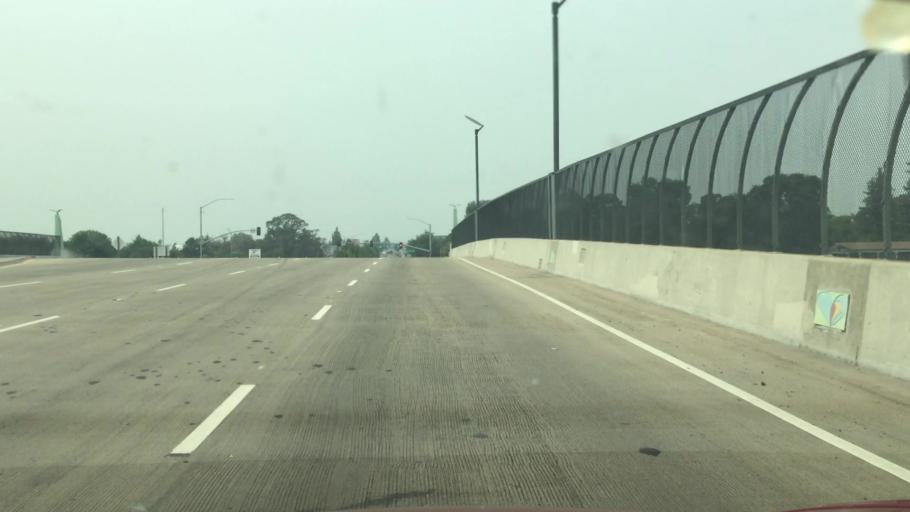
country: US
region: California
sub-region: San Joaquin County
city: Morada
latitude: 38.0214
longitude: -121.2578
